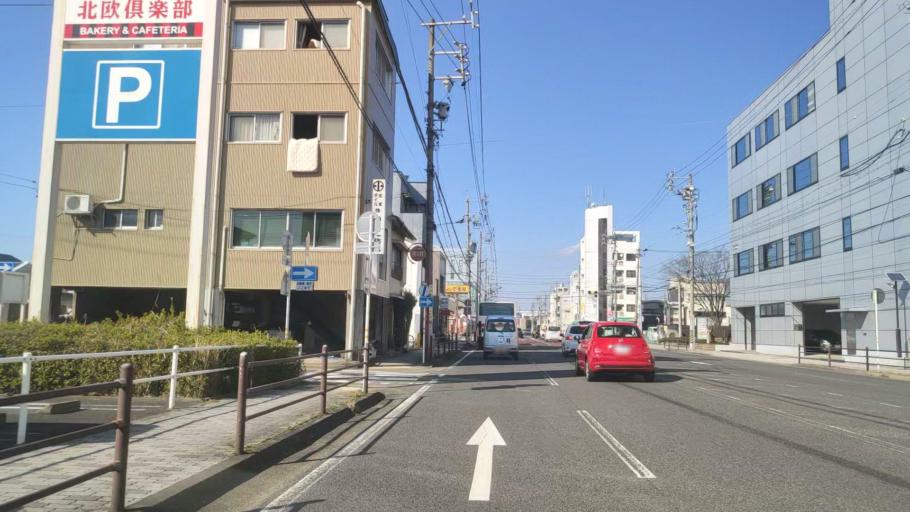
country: JP
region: Gifu
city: Gifu-shi
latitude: 35.4197
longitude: 136.7464
